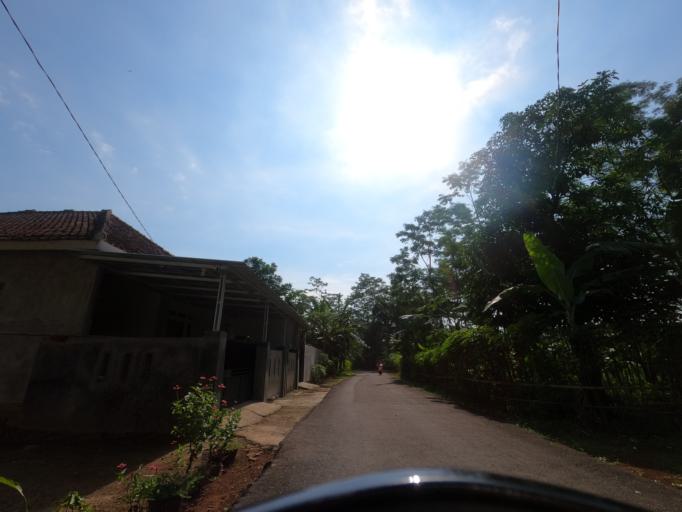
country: ID
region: West Java
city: Lembang
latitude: -6.5800
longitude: 107.7827
